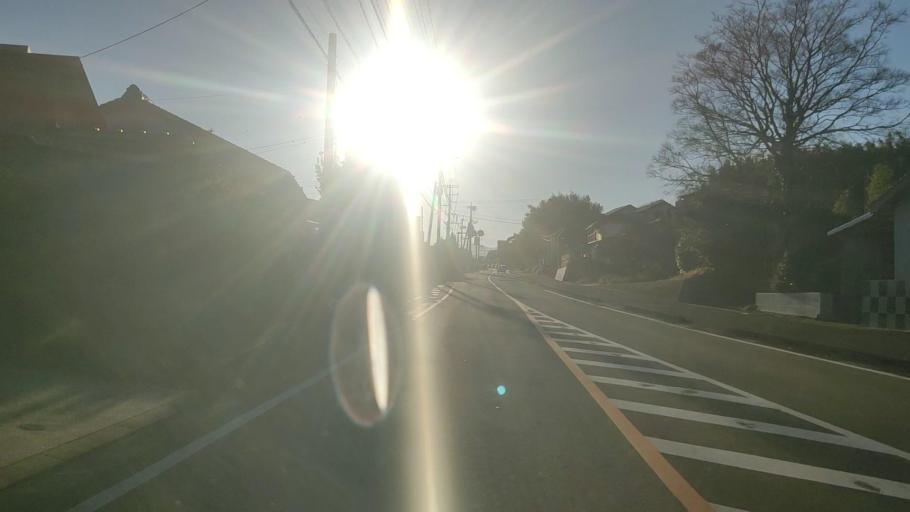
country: JP
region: Miyazaki
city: Miyazaki-shi
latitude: 31.8470
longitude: 131.3481
